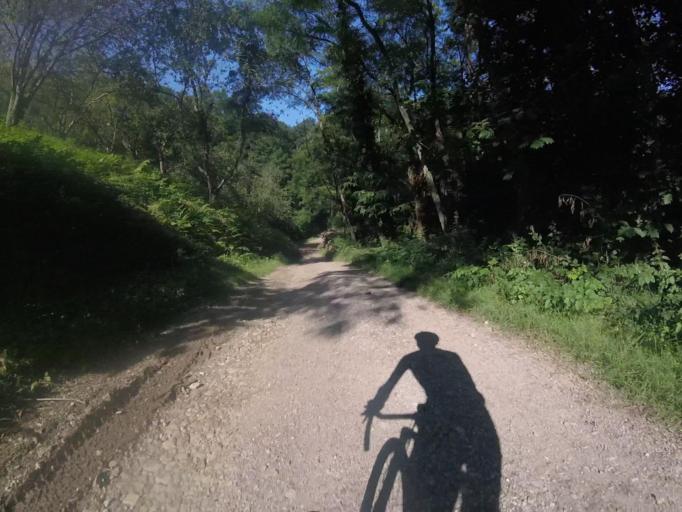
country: ES
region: Basque Country
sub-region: Provincia de Guipuzcoa
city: Astigarraga
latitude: 43.2631
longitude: -1.9371
